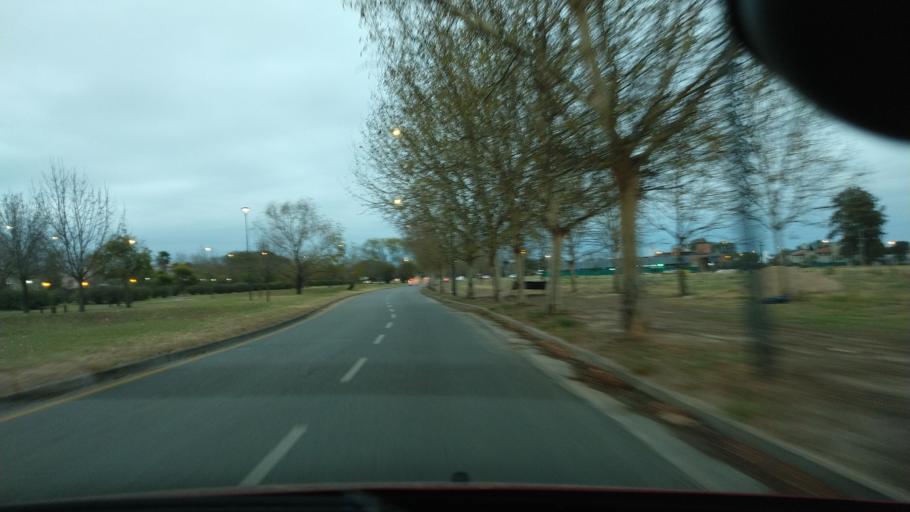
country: AR
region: Cordoba
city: La Calera
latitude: -31.3756
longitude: -64.2769
